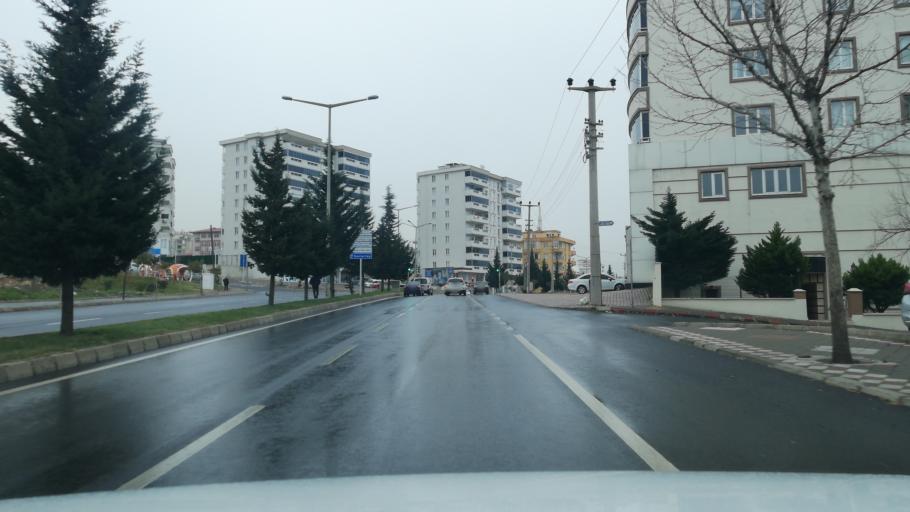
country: TR
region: Kahramanmaras
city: Kahramanmaras
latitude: 37.5912
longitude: 36.8815
